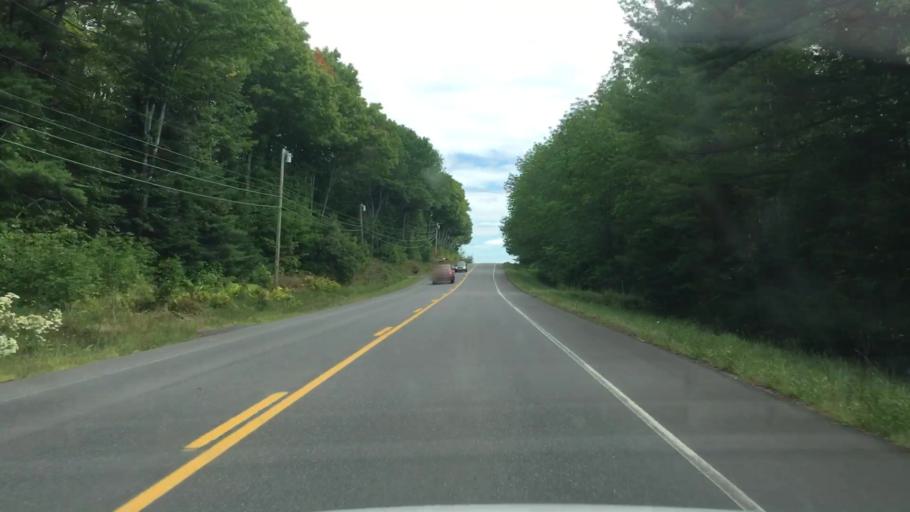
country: US
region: Maine
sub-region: Piscataquis County
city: Dover-Foxcroft
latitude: 45.2241
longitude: -69.1278
